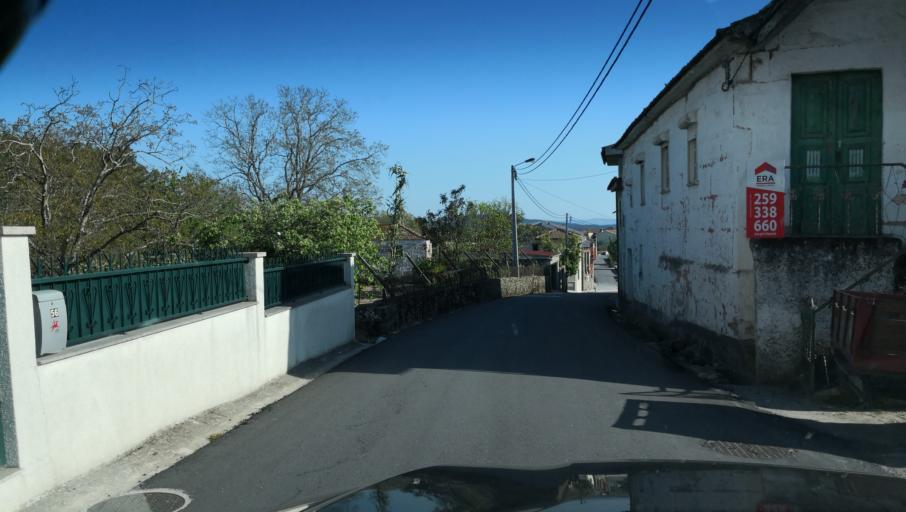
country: PT
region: Vila Real
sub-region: Vila Real
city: Vila Real
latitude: 41.2852
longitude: -7.6835
